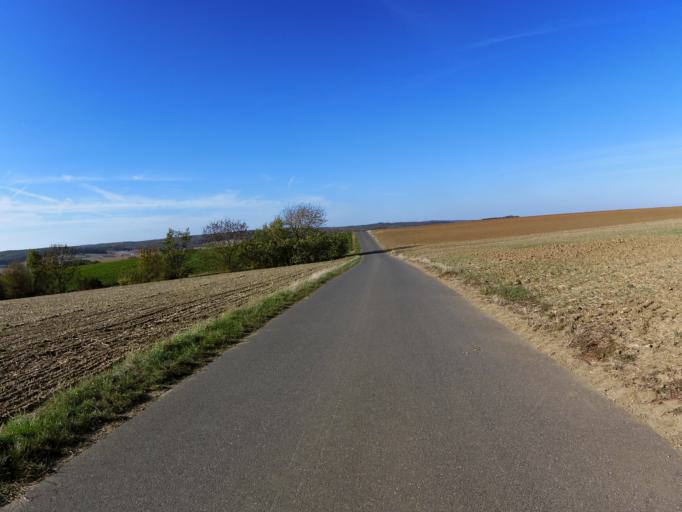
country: DE
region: Bavaria
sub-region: Regierungsbezirk Unterfranken
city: Reichenberg
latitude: 49.7153
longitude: 9.9364
